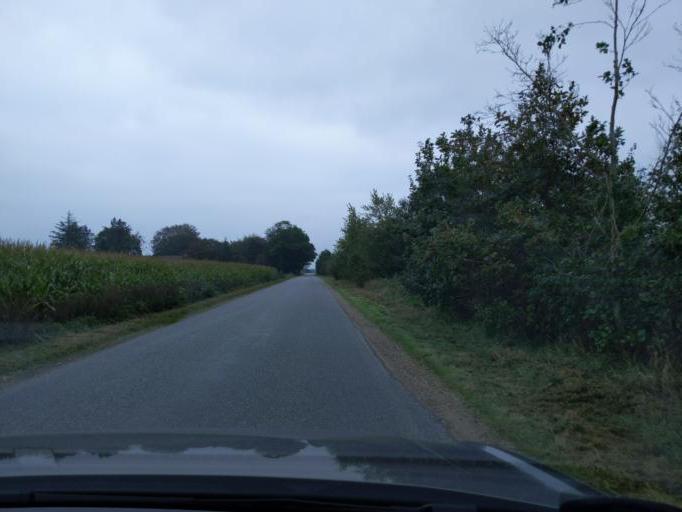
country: DK
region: Central Jutland
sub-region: Viborg Kommune
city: Karup
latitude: 56.3692
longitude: 9.2506
